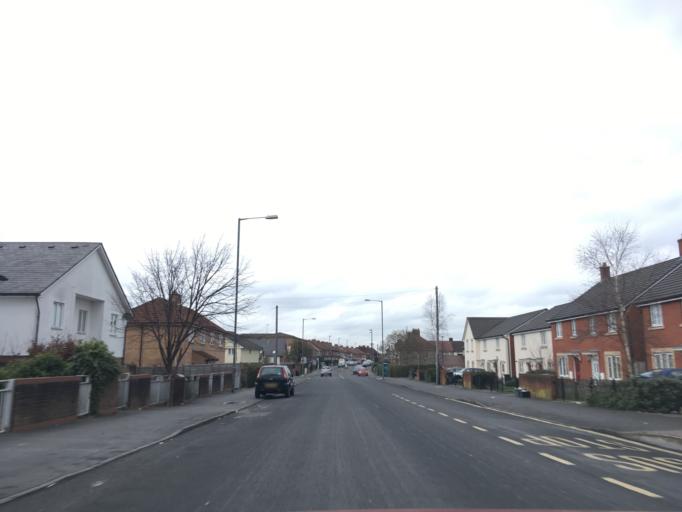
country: GB
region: England
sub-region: South Gloucestershire
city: Stoke Gifford
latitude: 51.4985
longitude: -2.5720
